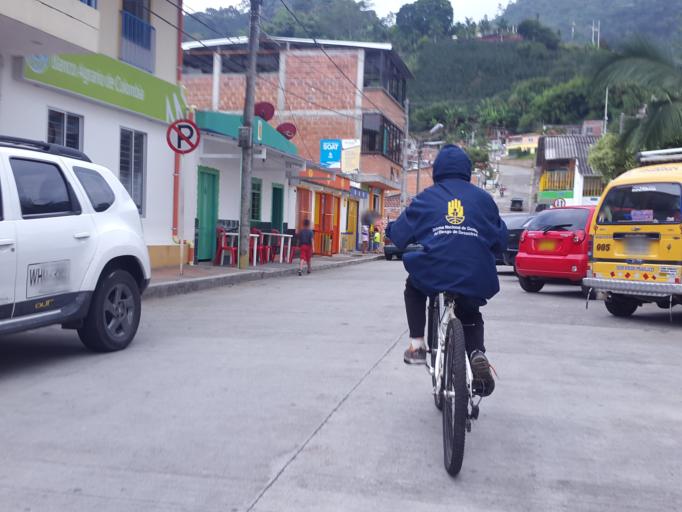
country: CO
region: Quindio
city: Buenavista
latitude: 4.3597
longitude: -75.7382
